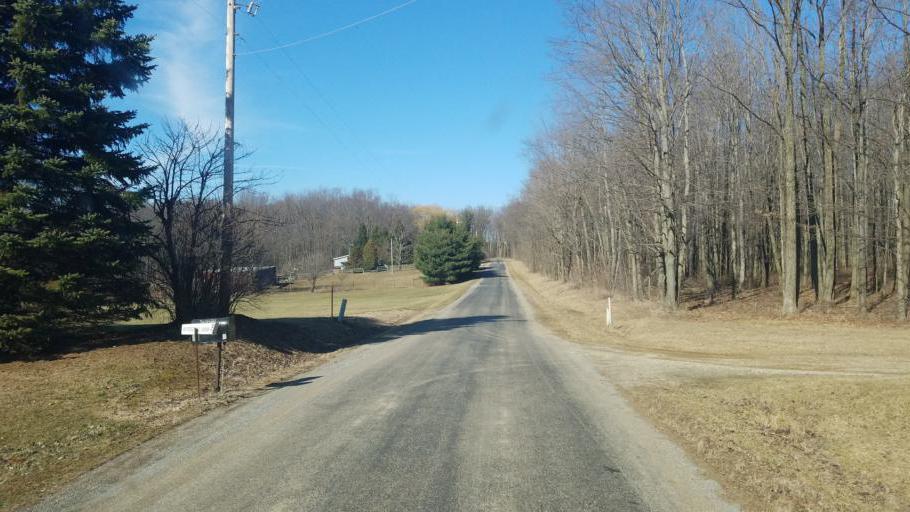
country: US
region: Ohio
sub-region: Sandusky County
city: Bellville
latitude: 40.5682
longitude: -82.5804
